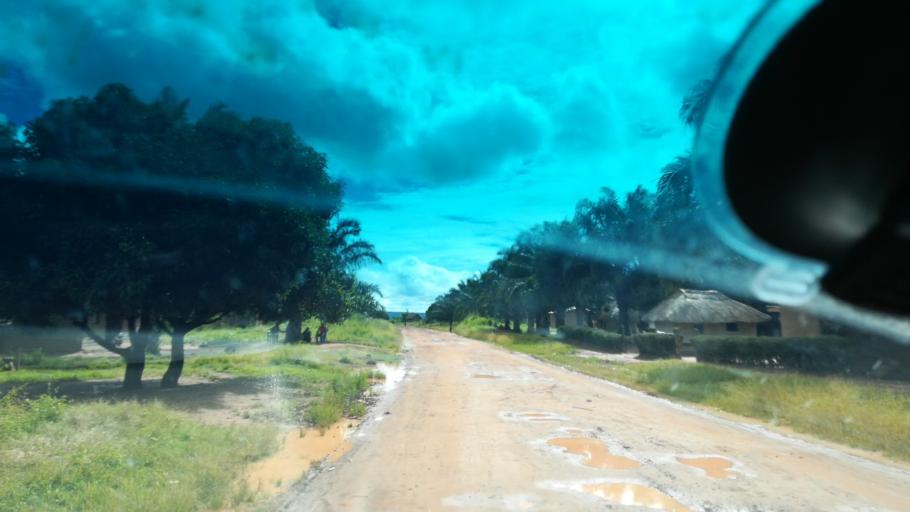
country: ZM
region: Luapula
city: Nchelenge
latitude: -9.1296
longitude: 28.3016
